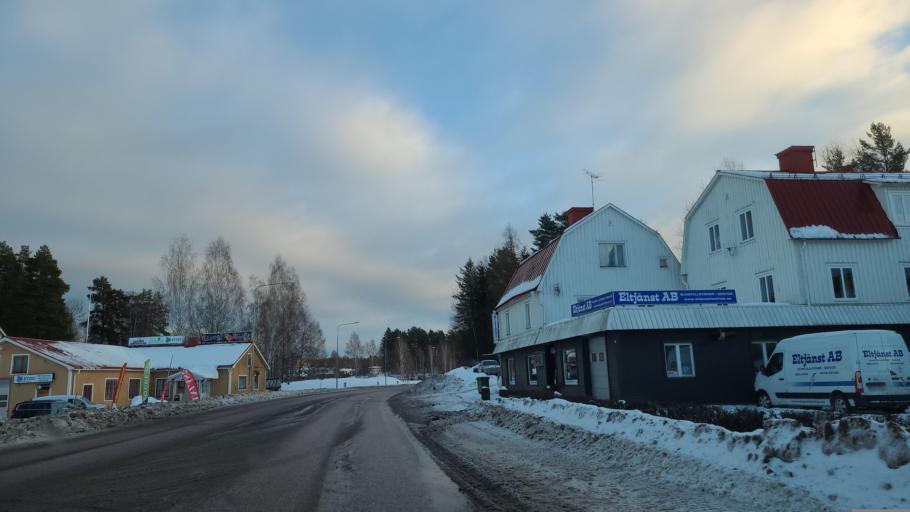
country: SE
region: Gaevleborg
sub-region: Bollnas Kommun
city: Bollnas
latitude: 61.3567
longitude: 16.4126
